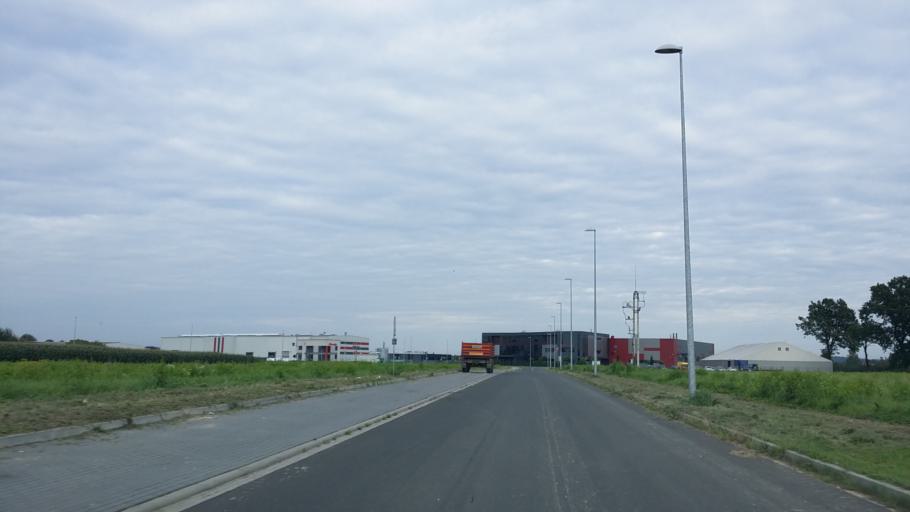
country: PL
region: Lesser Poland Voivodeship
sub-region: Powiat oswiecimski
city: Zator
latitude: 49.9958
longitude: 19.4134
